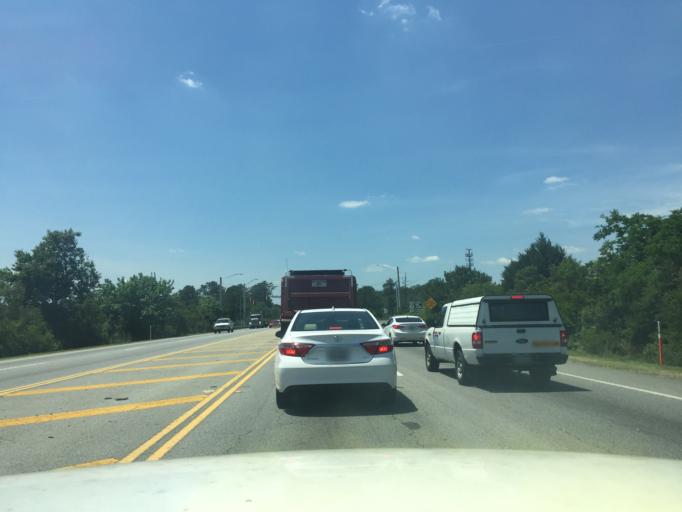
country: US
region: Georgia
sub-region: Chatham County
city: Georgetown
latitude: 32.0396
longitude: -81.2061
